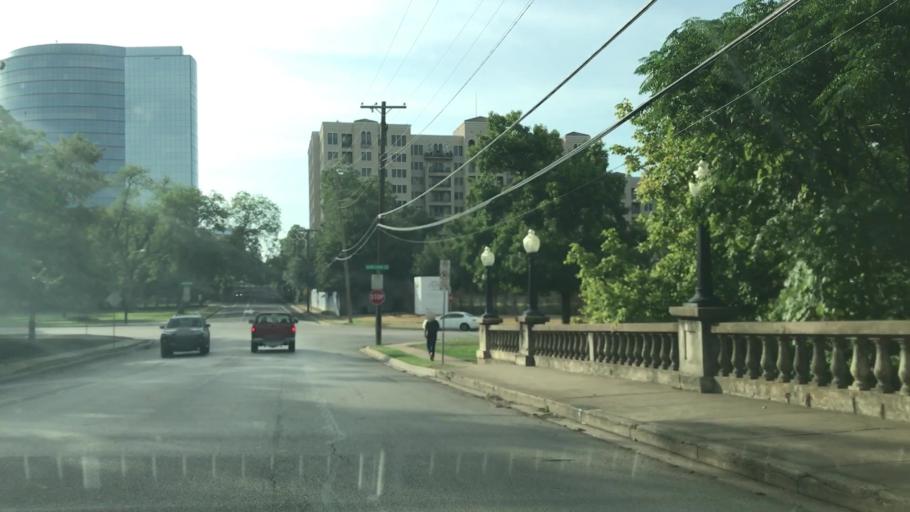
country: US
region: Texas
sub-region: Dallas County
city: Dallas
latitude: 32.8012
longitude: -96.8093
